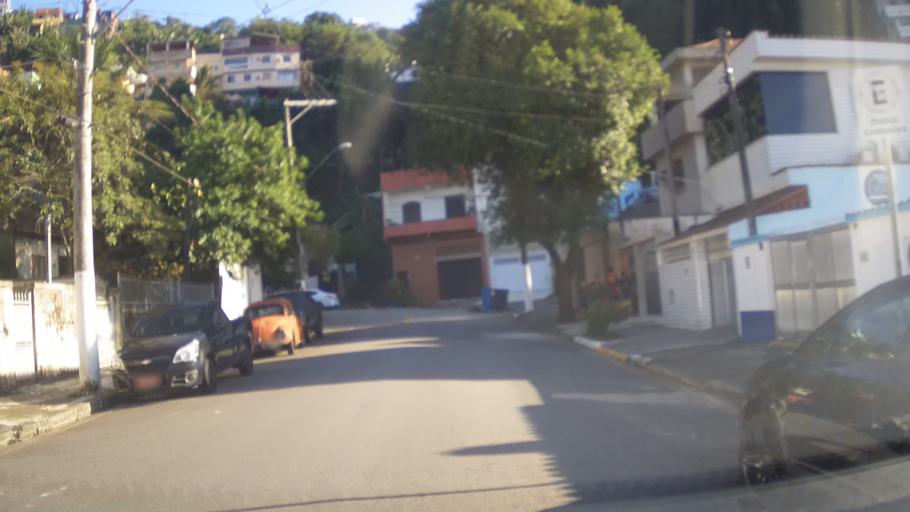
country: BR
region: Sao Paulo
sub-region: Santos
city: Santos
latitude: -23.9404
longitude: -46.3396
